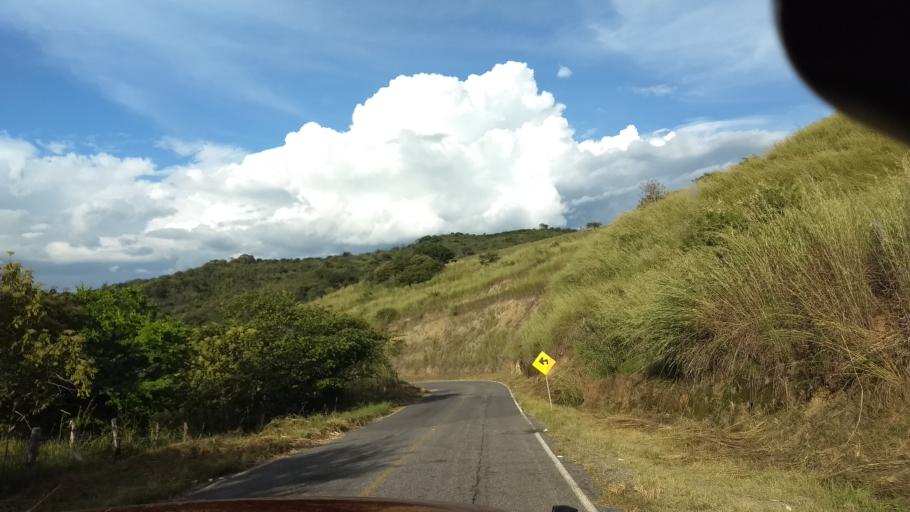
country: MX
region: Colima
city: Suchitlan
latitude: 19.4588
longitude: -103.7940
